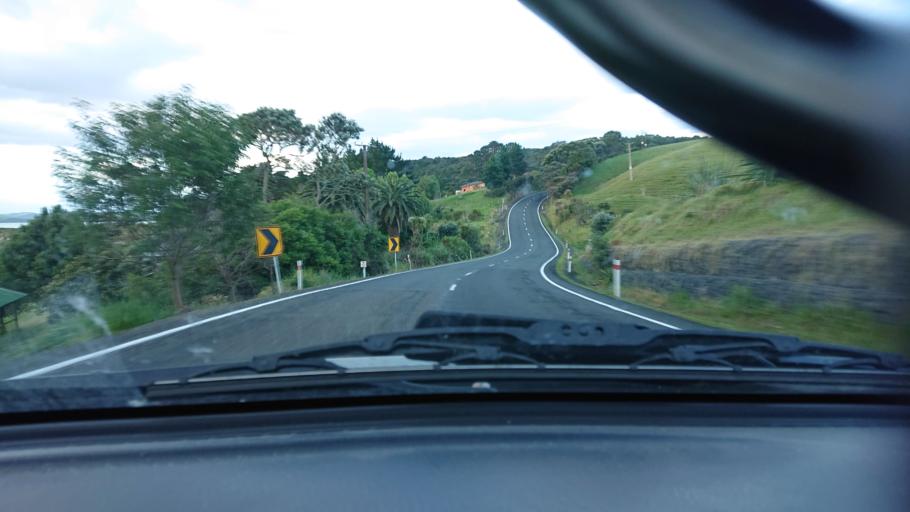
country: NZ
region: Auckland
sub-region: Auckland
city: Wellsford
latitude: -36.4398
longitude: 174.4319
